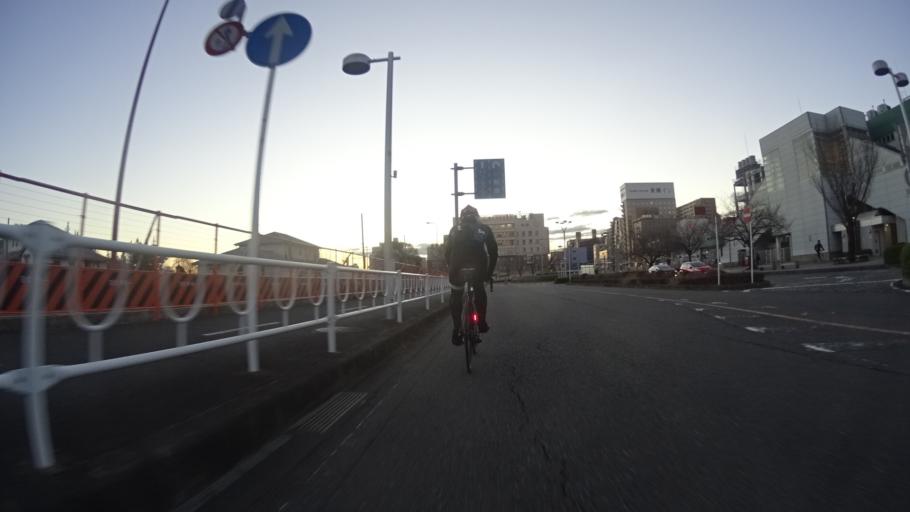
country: JP
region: Tokyo
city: Hachioji
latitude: 35.5823
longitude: 139.3712
